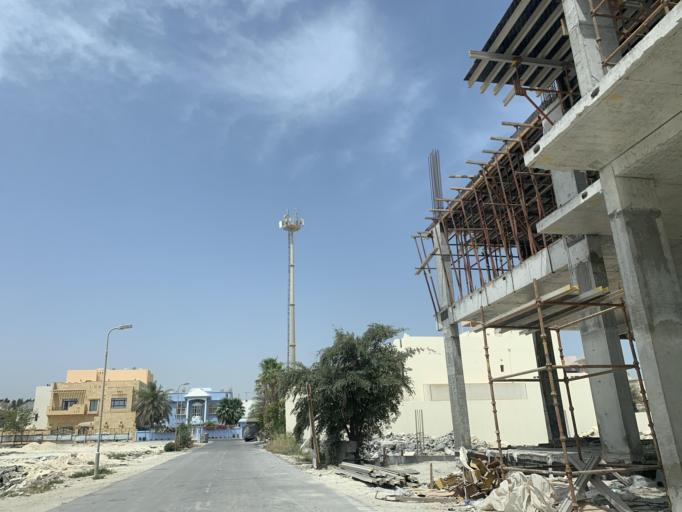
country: BH
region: Northern
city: Ar Rifa'
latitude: 26.1443
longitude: 50.5571
